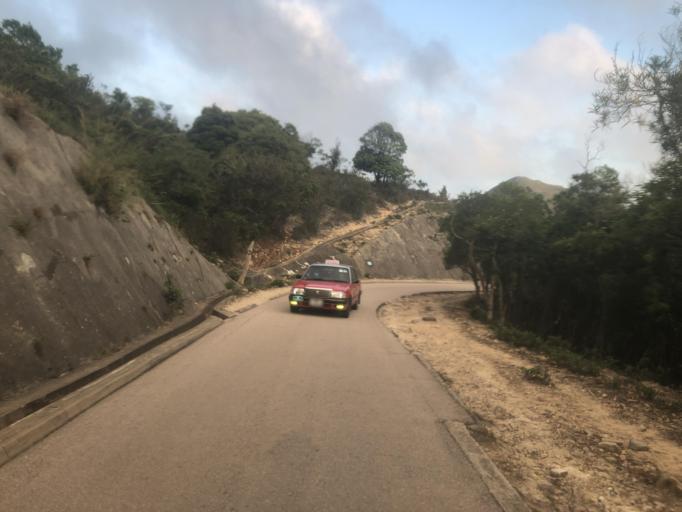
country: HK
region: Sai Kung
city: Sai Kung
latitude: 22.3623
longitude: 114.3502
